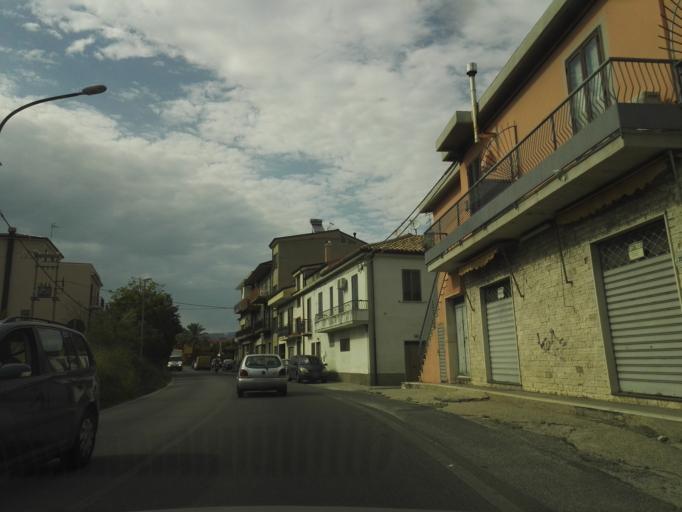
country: IT
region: Calabria
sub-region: Provincia di Catanzaro
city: Marina di Davoli
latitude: 38.6596
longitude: 16.5459
